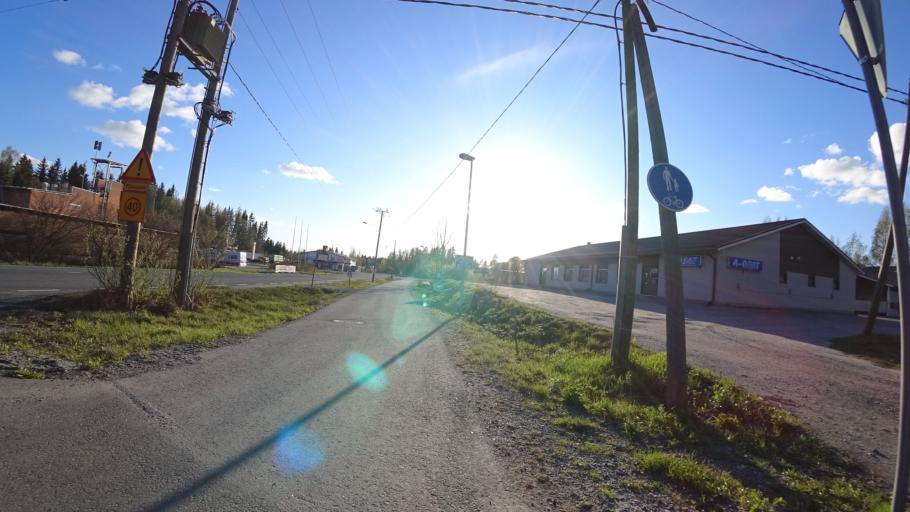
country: FI
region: Pirkanmaa
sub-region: Tampere
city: Nokia
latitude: 61.4953
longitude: 23.5357
